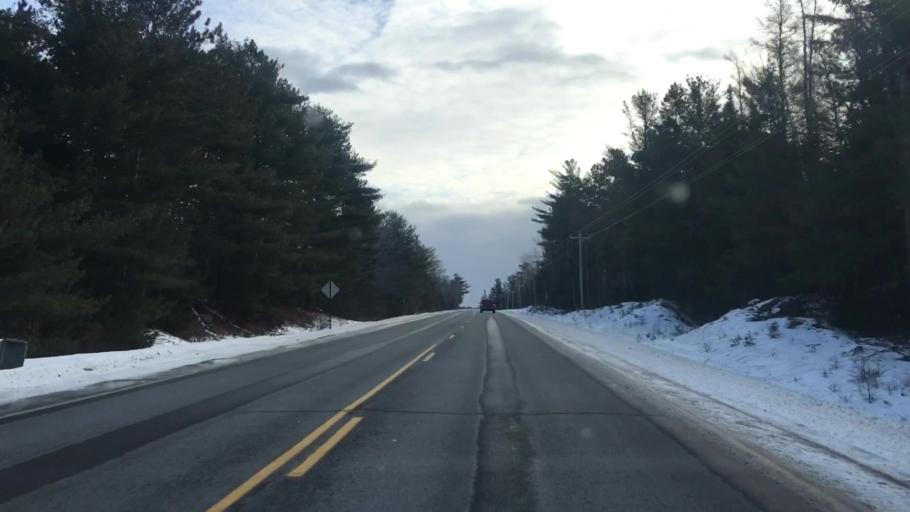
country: US
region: Maine
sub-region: Washington County
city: Machias
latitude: 44.9999
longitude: -67.5988
